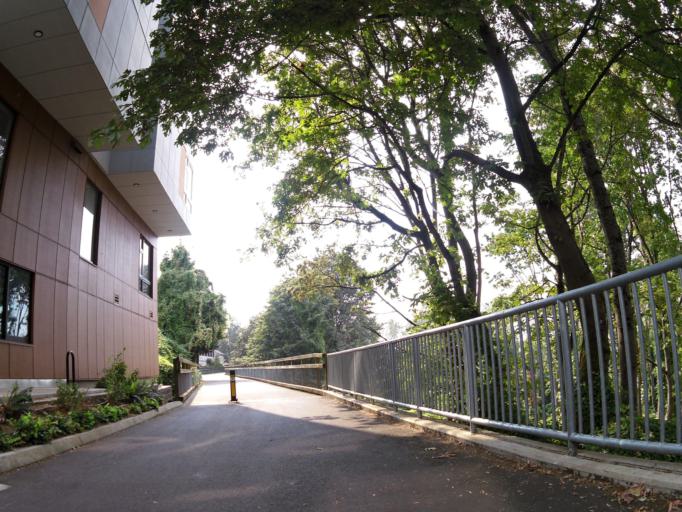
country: US
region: Washington
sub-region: Whatcom County
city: Bellingham
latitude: 48.7450
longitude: -122.4833
